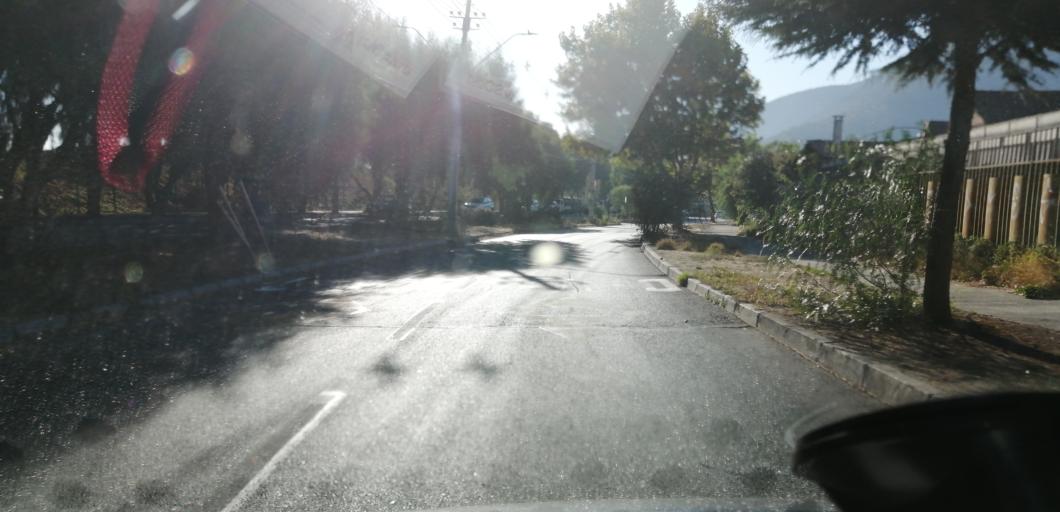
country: CL
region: Santiago Metropolitan
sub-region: Provincia de Santiago
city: Lo Prado
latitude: -33.4530
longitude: -70.8531
